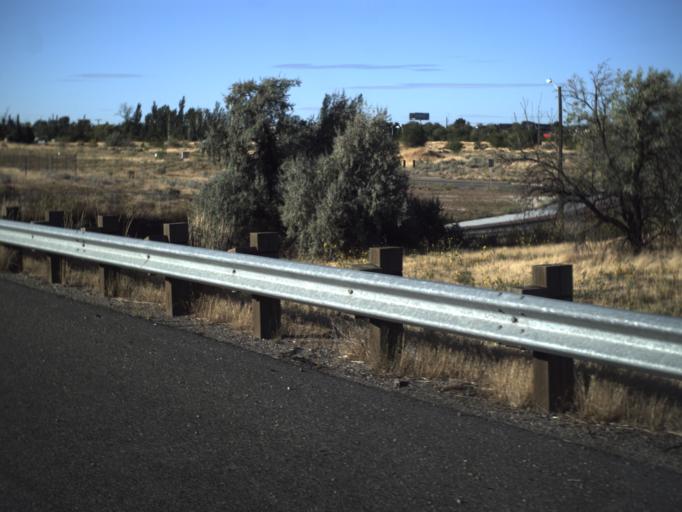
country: US
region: Utah
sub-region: Weber County
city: Riverdale
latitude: 41.1837
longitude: -112.0112
